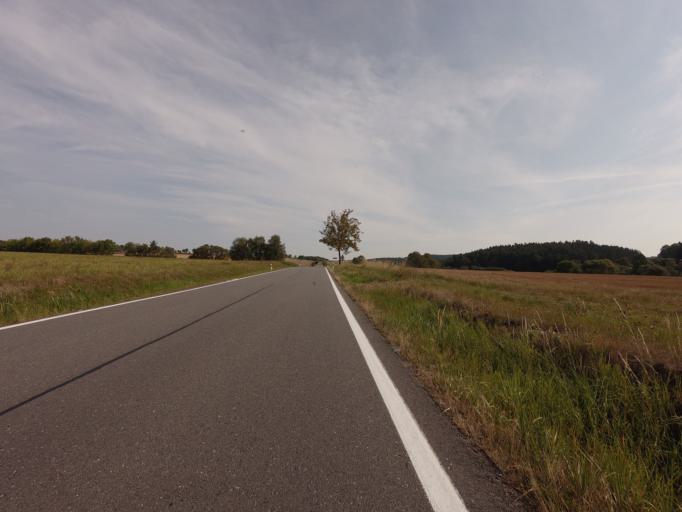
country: CZ
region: Jihocesky
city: Milevsko
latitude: 49.4741
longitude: 14.3644
